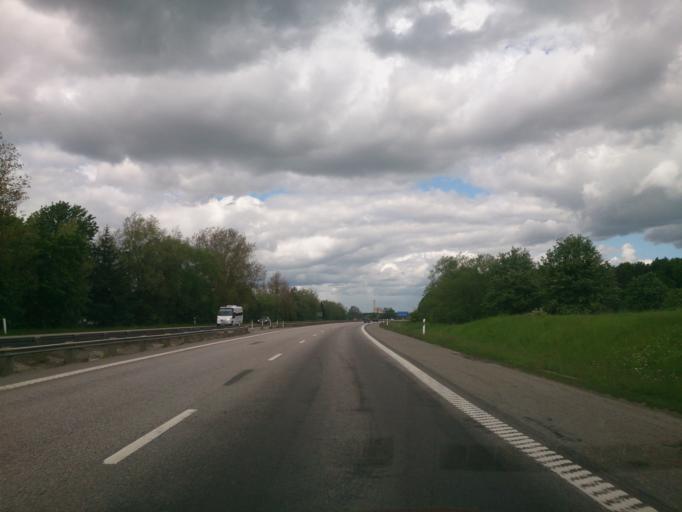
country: SE
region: OEstergoetland
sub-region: Norrkopings Kommun
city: Norrkoping
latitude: 58.5693
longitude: 16.2162
